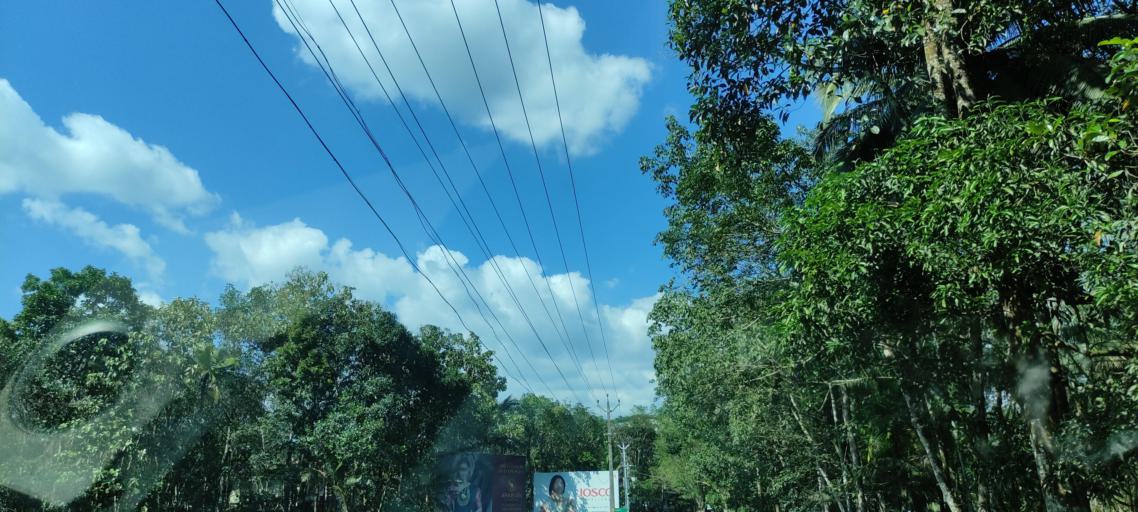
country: IN
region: Kerala
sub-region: Pattanamtitta
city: Adur
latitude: 9.1911
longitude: 76.7454
